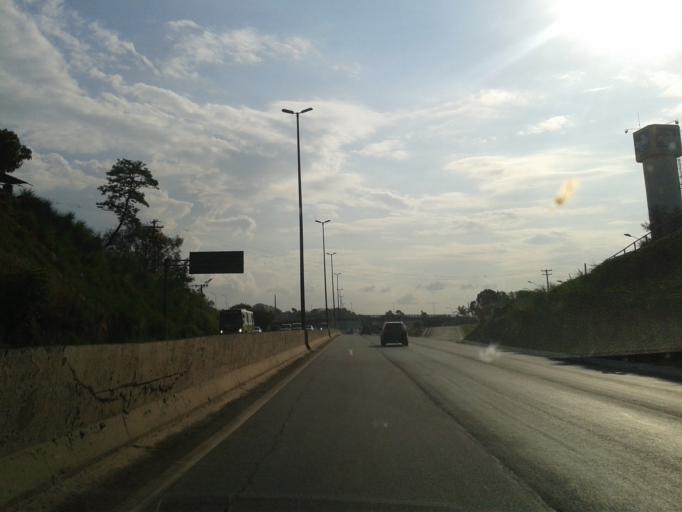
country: BR
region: Minas Gerais
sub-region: Belo Horizonte
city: Belo Horizonte
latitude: -19.8677
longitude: -43.9353
